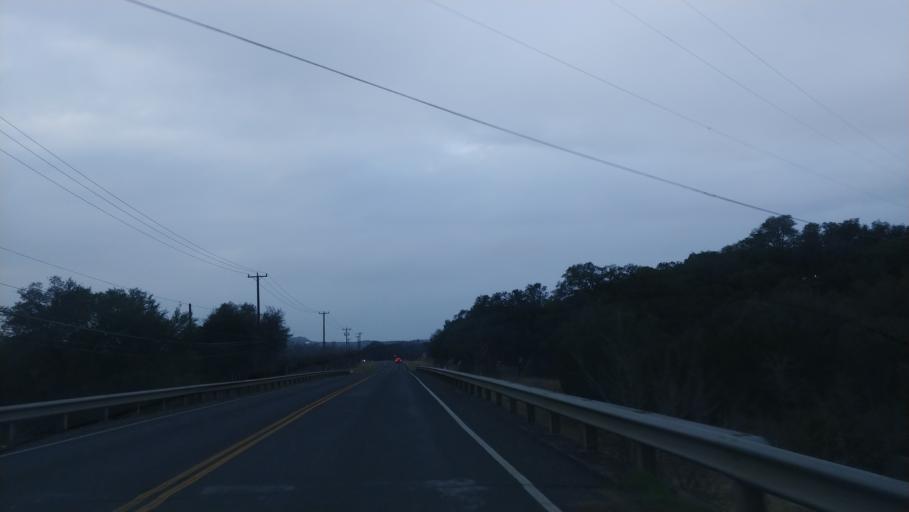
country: US
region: Texas
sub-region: Bexar County
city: Scenic Oaks
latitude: 29.6784
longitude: -98.6671
